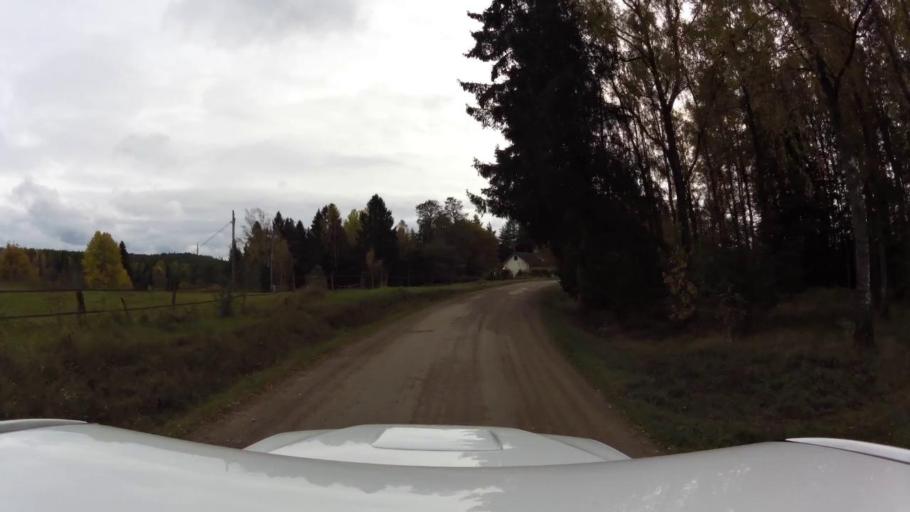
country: SE
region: OEstergoetland
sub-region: Linkopings Kommun
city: Ekangen
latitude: 58.5558
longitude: 15.6635
